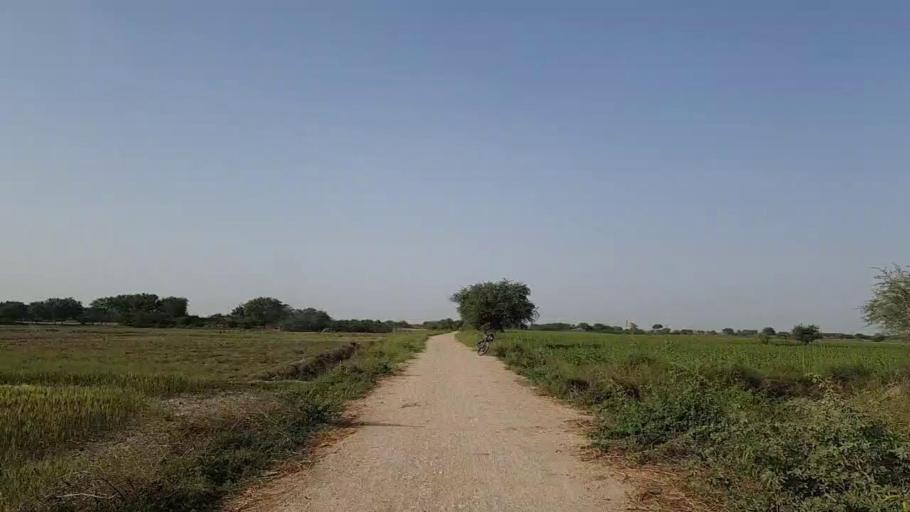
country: PK
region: Sindh
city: Jati
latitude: 24.2873
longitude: 68.1491
